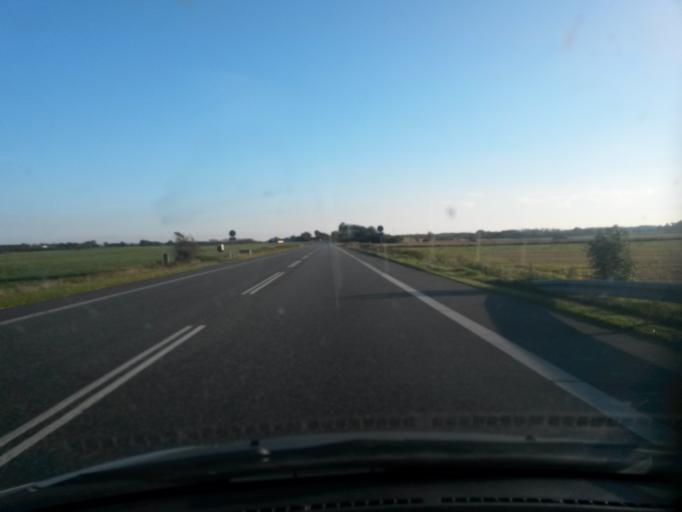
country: DK
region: Central Jutland
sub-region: Silkeborg Kommune
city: Kjellerup
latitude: 56.2860
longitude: 9.3205
